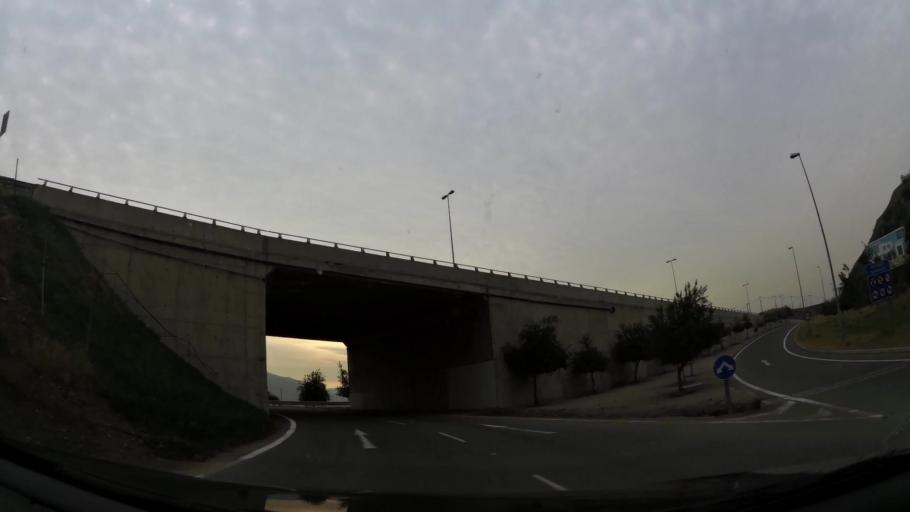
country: CL
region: Santiago Metropolitan
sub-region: Provincia de Chacabuco
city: Chicureo Abajo
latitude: -33.3211
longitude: -70.6255
